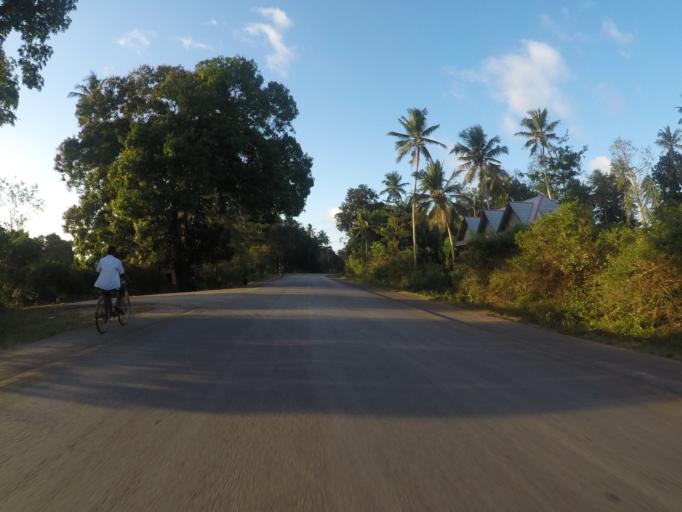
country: TZ
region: Zanzibar Central/South
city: Koani
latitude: -6.1758
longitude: 39.3295
